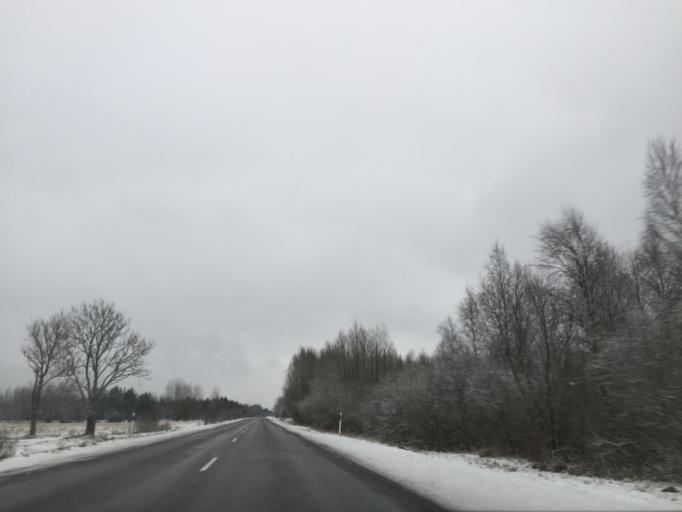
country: EE
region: Laeaene
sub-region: Lihula vald
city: Lihula
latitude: 58.6267
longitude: 23.8849
